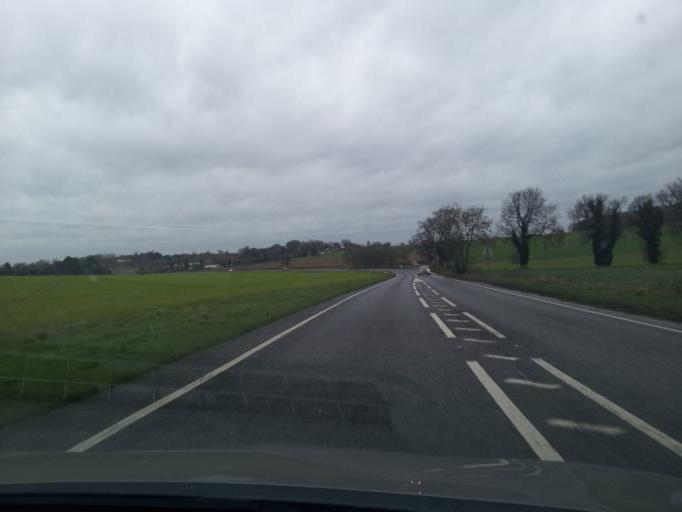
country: GB
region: England
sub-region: Suffolk
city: Botesdale
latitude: 52.3369
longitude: 0.9705
